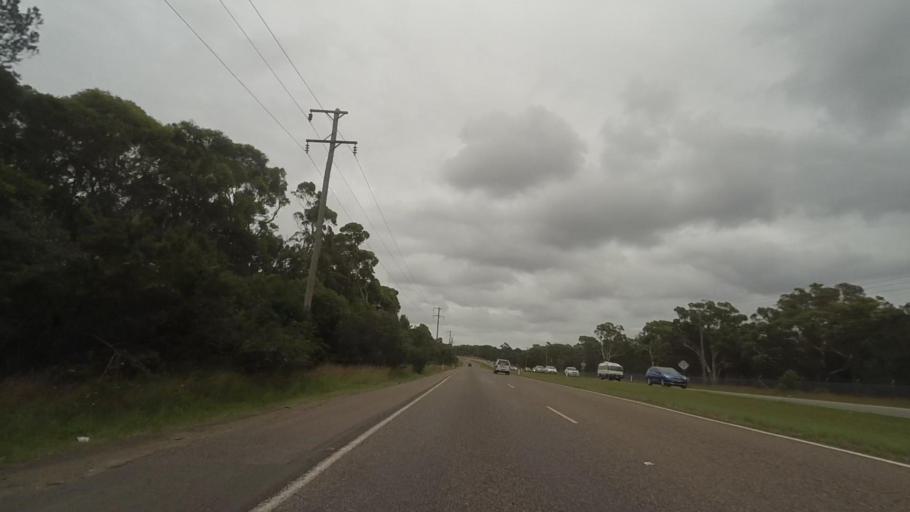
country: AU
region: New South Wales
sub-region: Wyong Shire
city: Kingfisher Shores
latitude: -33.1875
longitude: 151.5317
